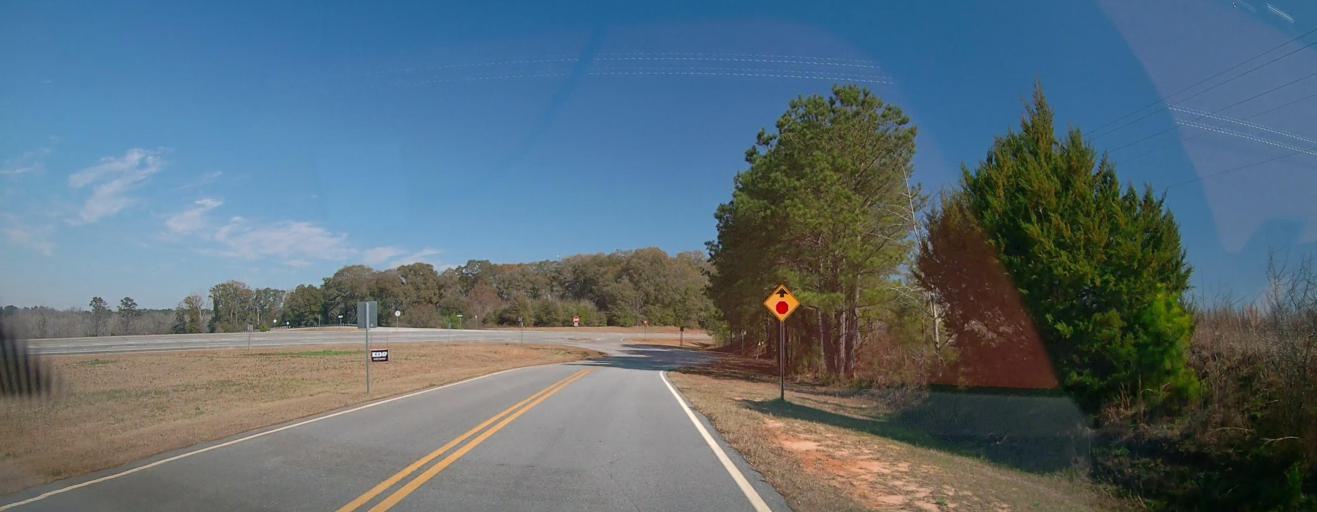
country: US
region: Georgia
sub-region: Houston County
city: Perry
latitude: 32.4387
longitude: -83.7289
